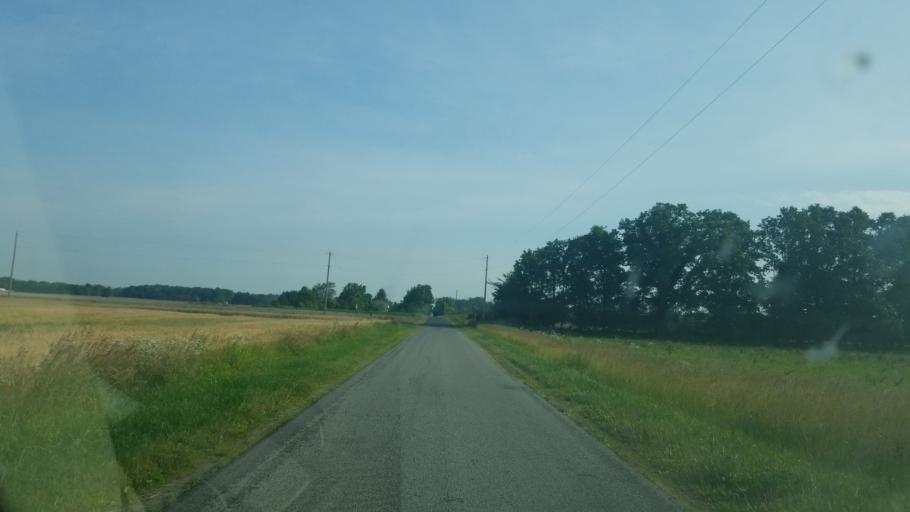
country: US
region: Ohio
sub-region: Hancock County
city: Arlington
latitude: 40.8477
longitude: -83.6702
